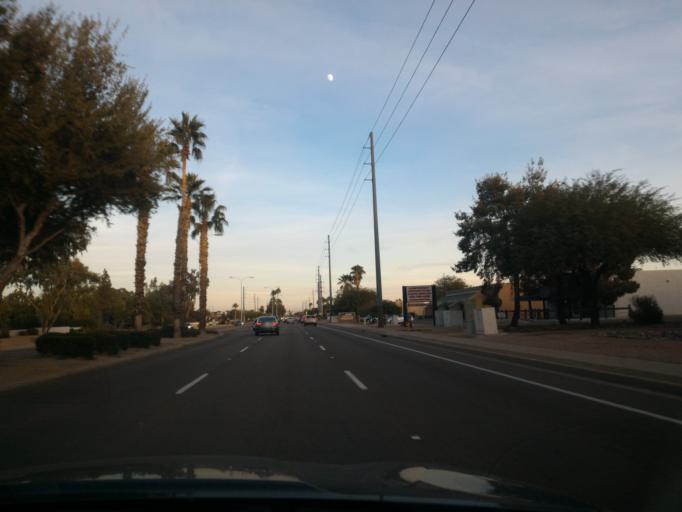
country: US
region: Arizona
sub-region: Maricopa County
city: Guadalupe
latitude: 33.3053
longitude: -111.9528
